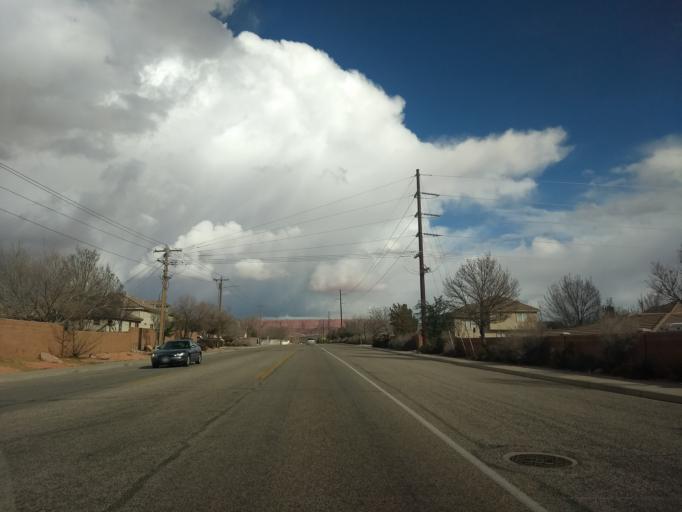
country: US
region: Utah
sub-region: Washington County
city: Saint George
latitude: 37.0667
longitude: -113.5407
